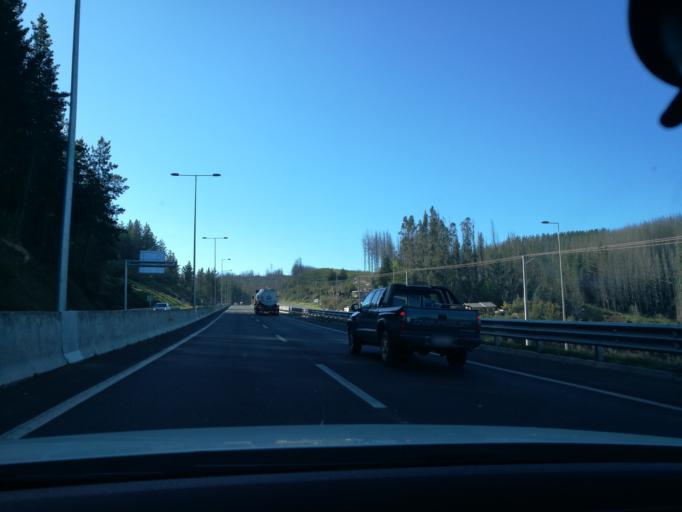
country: CL
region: Biobio
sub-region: Provincia de Concepcion
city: Penco
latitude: -36.8569
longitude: -72.8675
